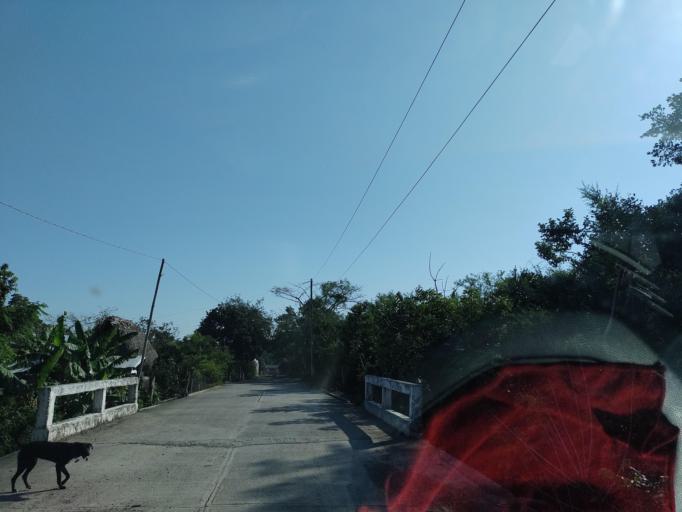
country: MX
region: Veracruz
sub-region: Papantla
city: Polutla
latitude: 20.4566
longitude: -97.2267
